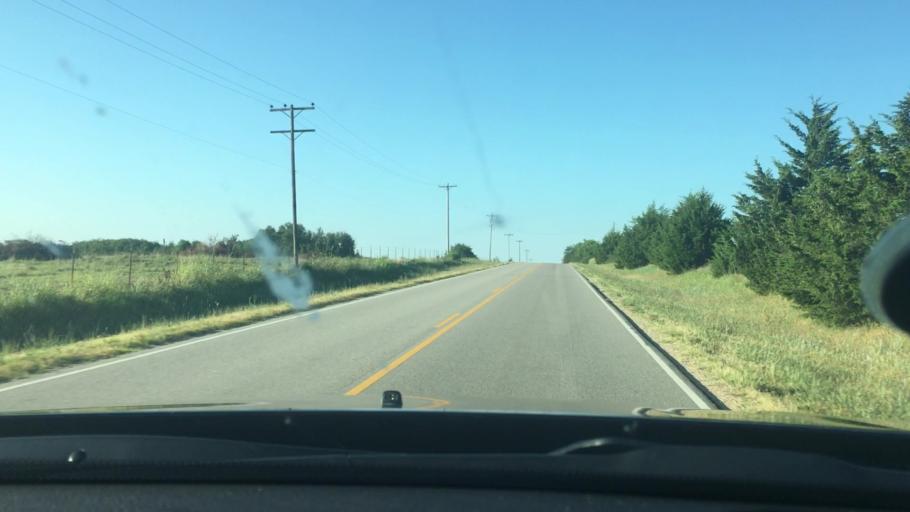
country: US
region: Oklahoma
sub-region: Murray County
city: Sulphur
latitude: 34.6112
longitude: -96.8449
